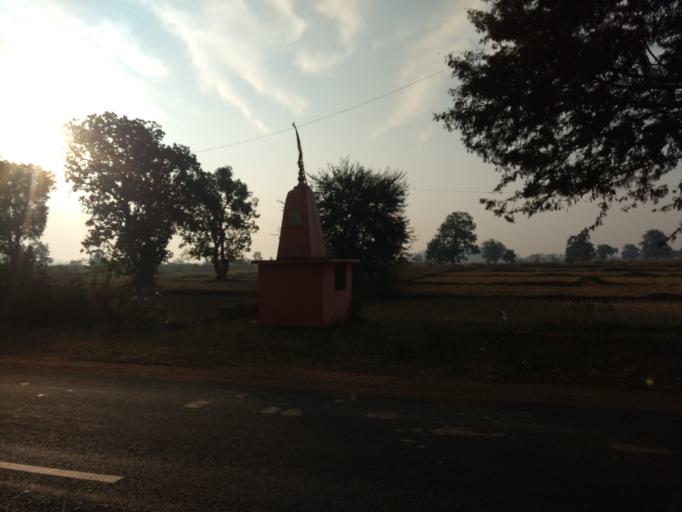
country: IN
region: Maharashtra
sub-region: Chandrapur
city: Mul
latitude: 19.9469
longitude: 79.9103
